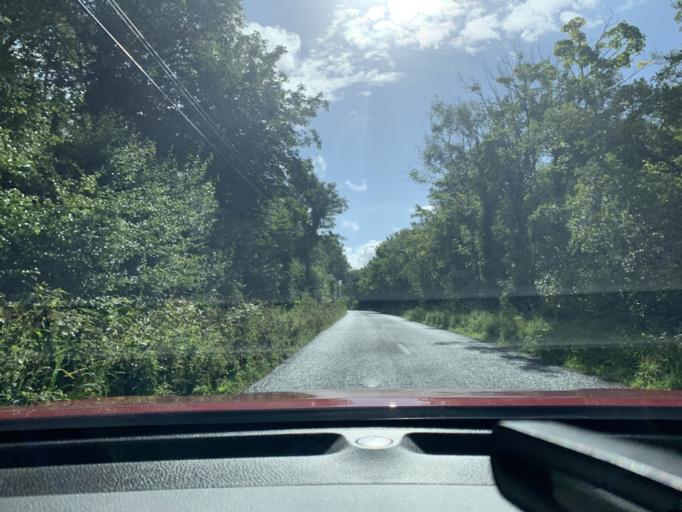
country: IE
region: Connaught
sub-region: Sligo
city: Strandhill
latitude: 54.3564
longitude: -8.5776
